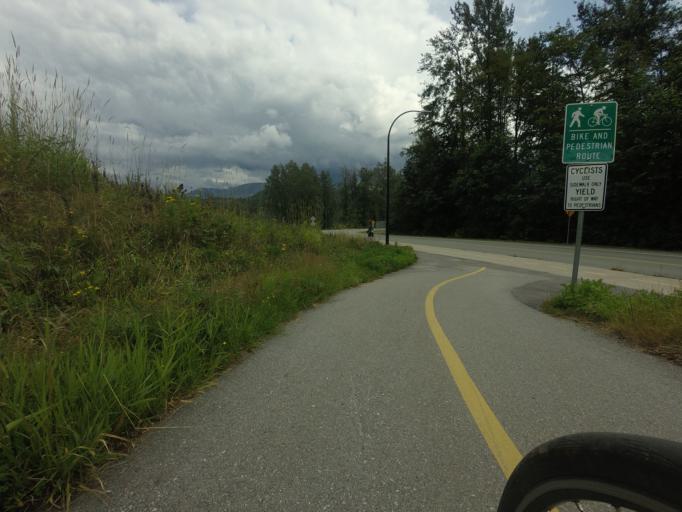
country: CA
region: British Columbia
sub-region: Greater Vancouver Regional District
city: Lions Bay
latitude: 49.7282
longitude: -123.1420
